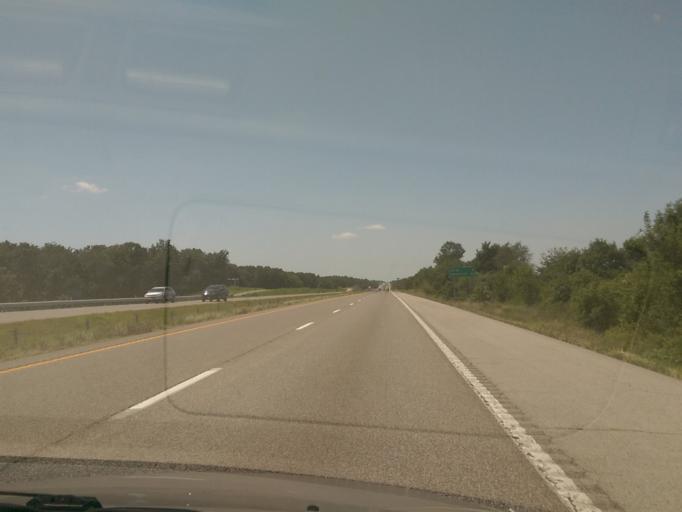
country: US
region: Missouri
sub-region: Saline County
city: Marshall
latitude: 38.9541
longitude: -93.1014
